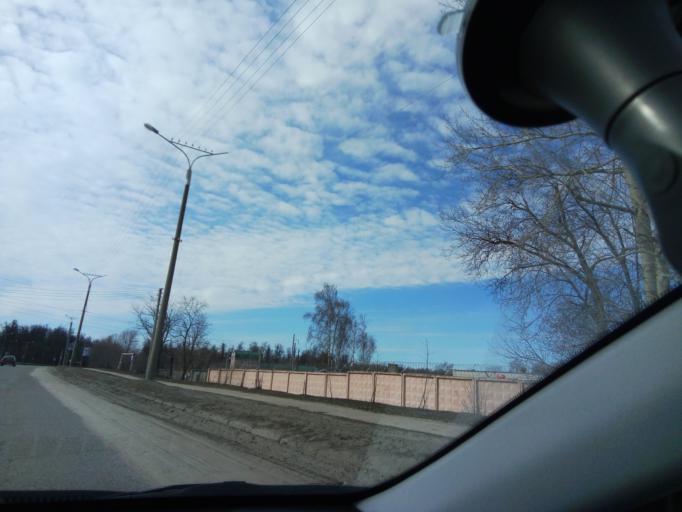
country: RU
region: Chuvashia
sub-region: Cheboksarskiy Rayon
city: Cheboksary
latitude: 56.0955
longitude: 47.2631
